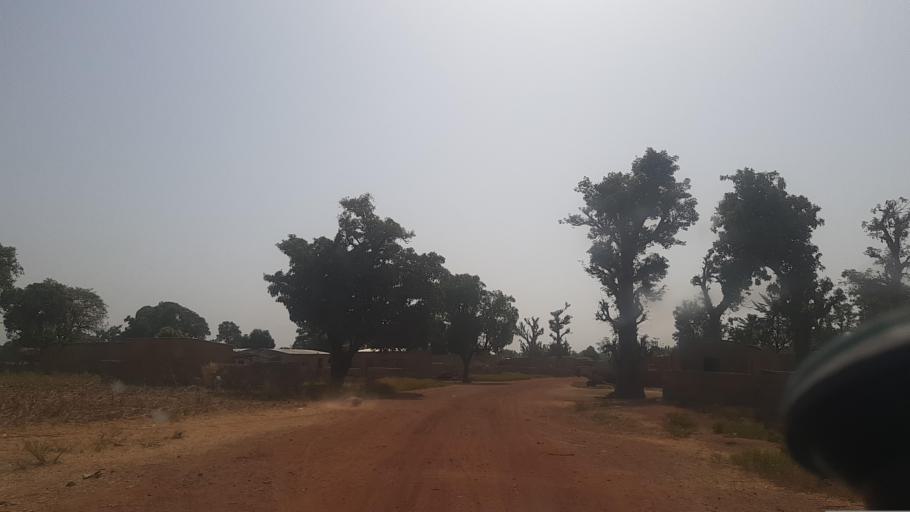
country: ML
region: Segou
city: Baroueli
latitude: 13.0140
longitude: -6.4234
